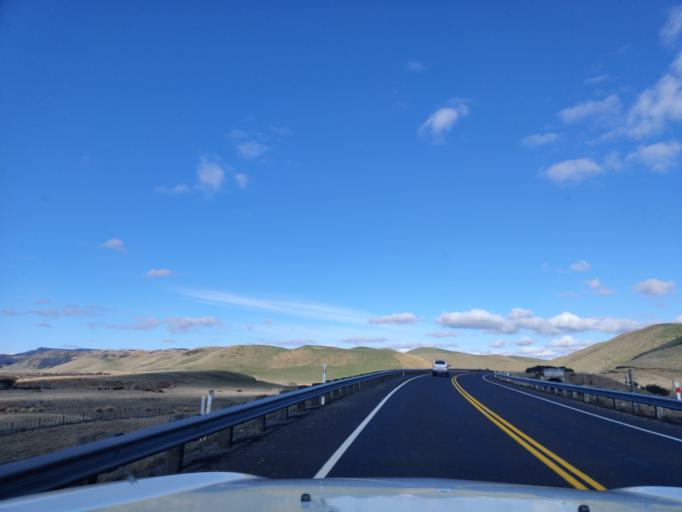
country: NZ
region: Manawatu-Wanganui
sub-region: Ruapehu District
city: Waiouru
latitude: -39.4980
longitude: 175.6738
